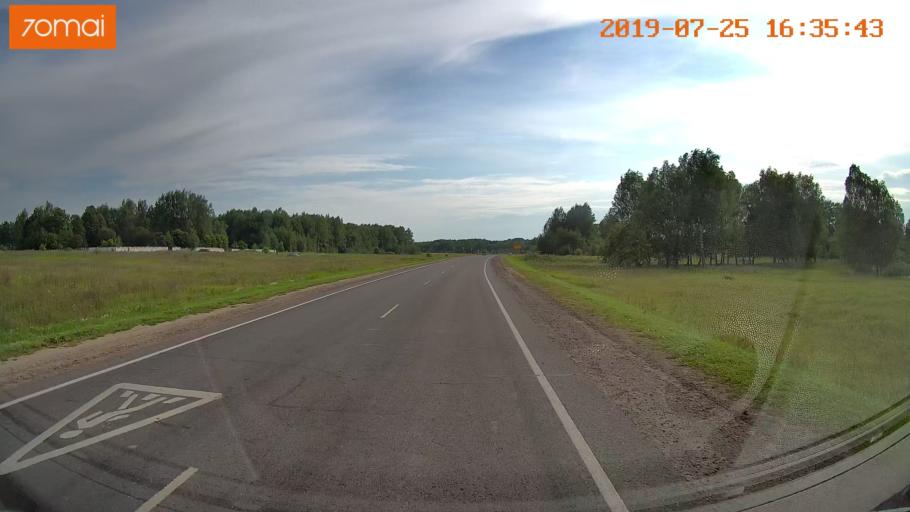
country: RU
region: Ivanovo
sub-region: Privolzhskiy Rayon
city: Ples
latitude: 57.4022
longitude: 41.4173
